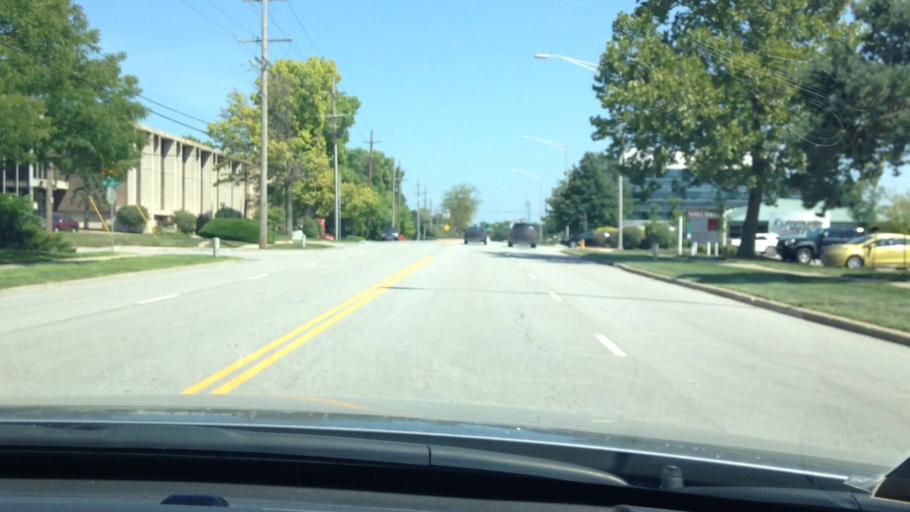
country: US
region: Kansas
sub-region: Johnson County
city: Overland Park
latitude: 38.9568
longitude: -94.6519
